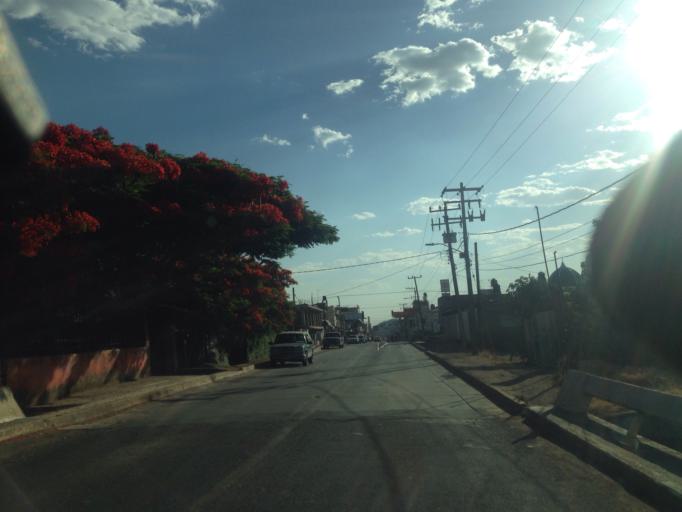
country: MX
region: Jalisco
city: Atotonilco el Alto
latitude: 20.5492
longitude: -102.5053
